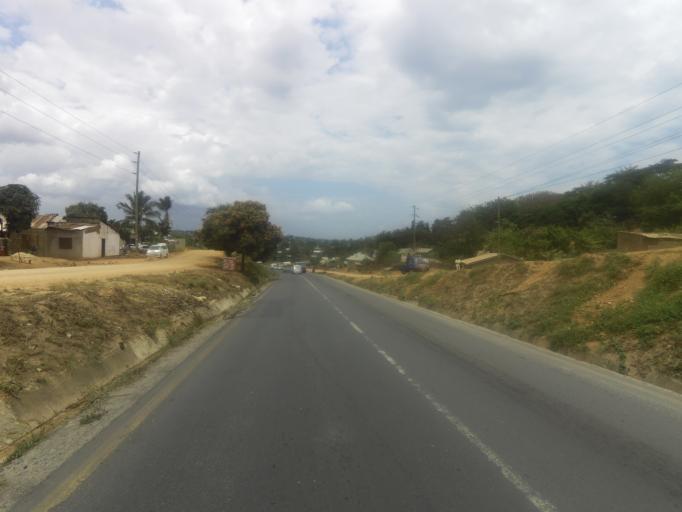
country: TZ
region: Pwani
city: Vikindu
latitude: -6.9327
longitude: 39.2723
